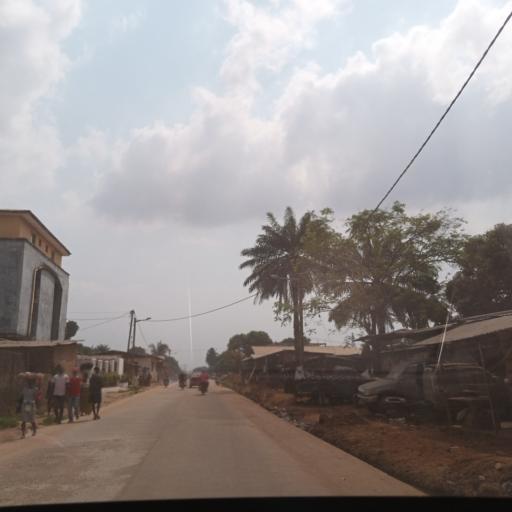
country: LR
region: Montserrado
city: Monrovia
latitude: 6.2880
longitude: -10.6899
